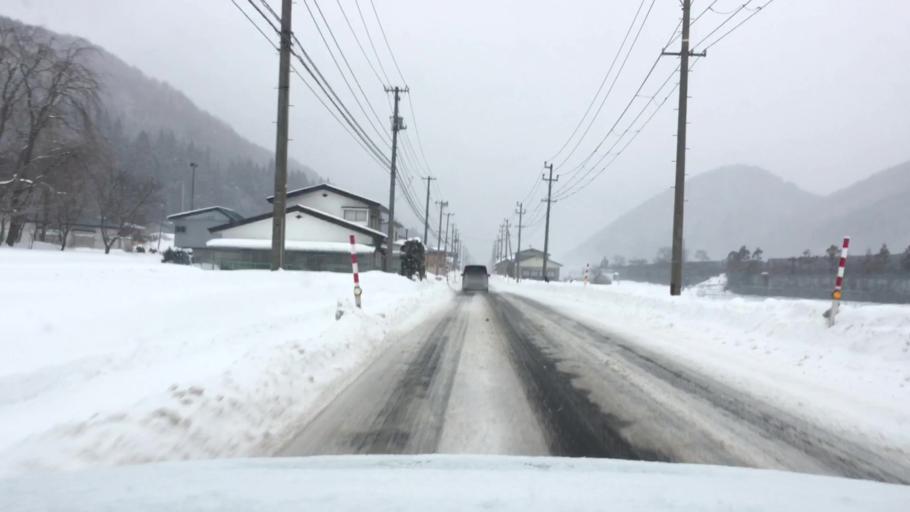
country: JP
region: Akita
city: Hanawa
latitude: 40.0680
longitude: 141.0168
